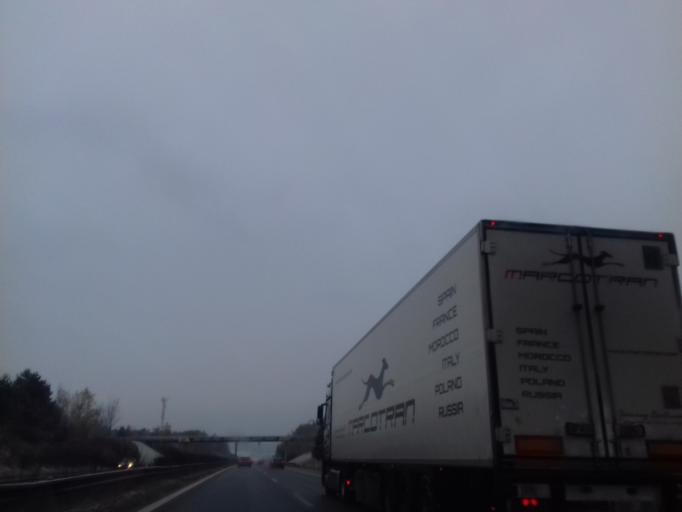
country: CZ
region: Central Bohemia
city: Zebrak
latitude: 49.8580
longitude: 13.8791
